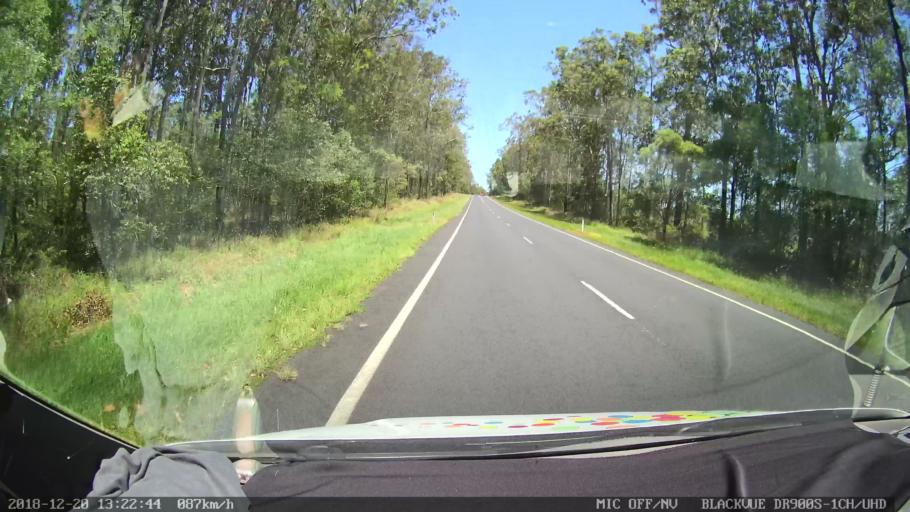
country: AU
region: New South Wales
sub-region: Richmond Valley
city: Casino
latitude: -29.0953
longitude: 153.0012
